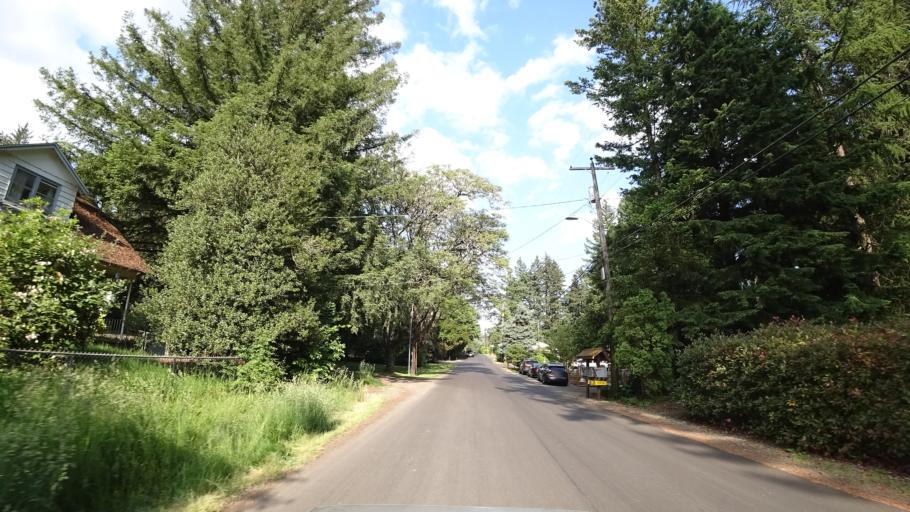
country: US
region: Oregon
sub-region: Washington County
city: Garden Home-Whitford
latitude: 45.4603
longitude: -122.7559
